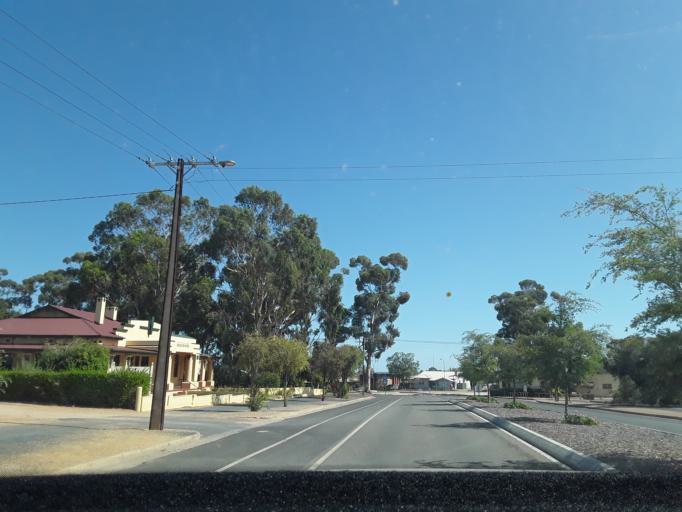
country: AU
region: South Australia
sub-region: Berri and Barmera
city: Barmera
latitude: -34.2537
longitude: 140.4654
